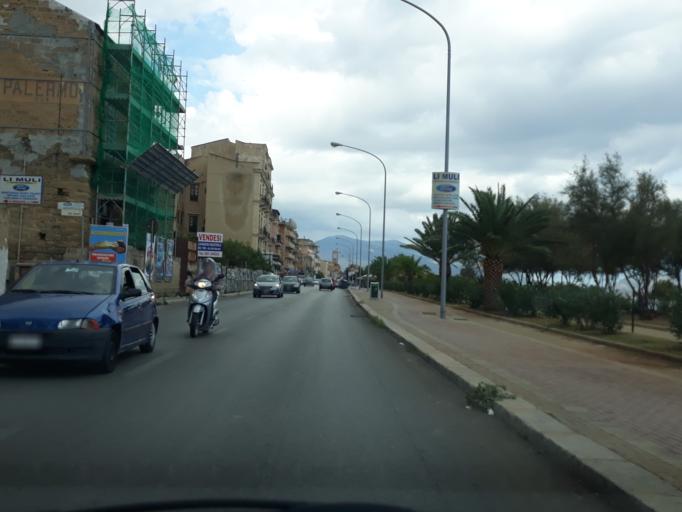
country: IT
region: Sicily
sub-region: Palermo
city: Ciaculli
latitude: 38.1033
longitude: 13.3934
